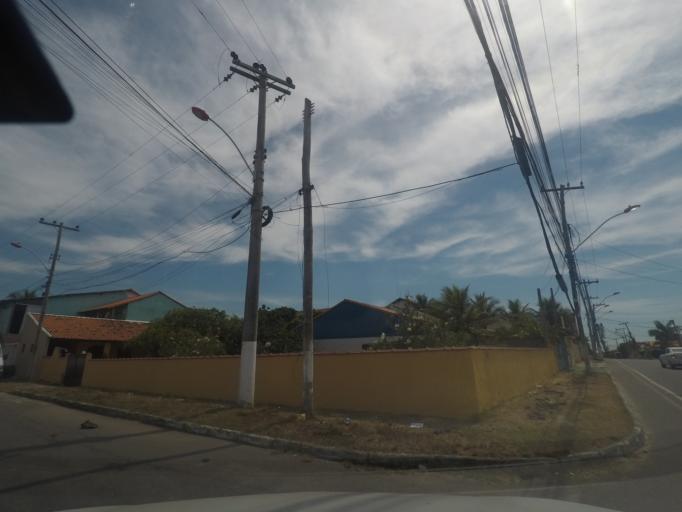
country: BR
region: Rio de Janeiro
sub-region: Marica
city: Marica
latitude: -22.9560
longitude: -42.7487
